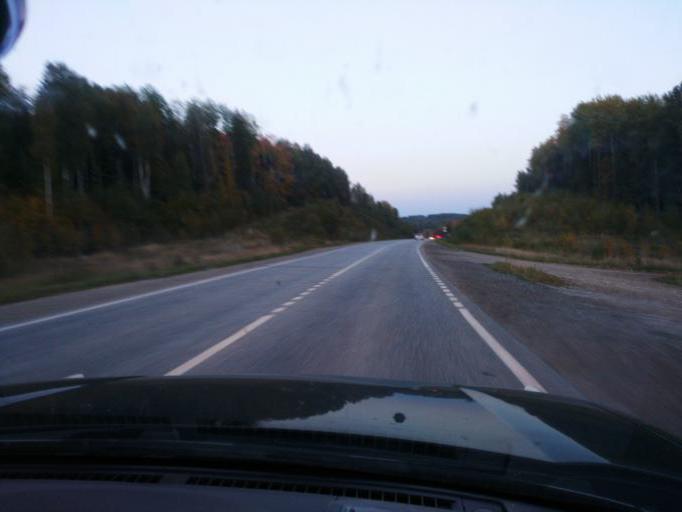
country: RU
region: Perm
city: Verkhnechusovskiye Gorodki
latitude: 58.2957
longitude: 56.8679
